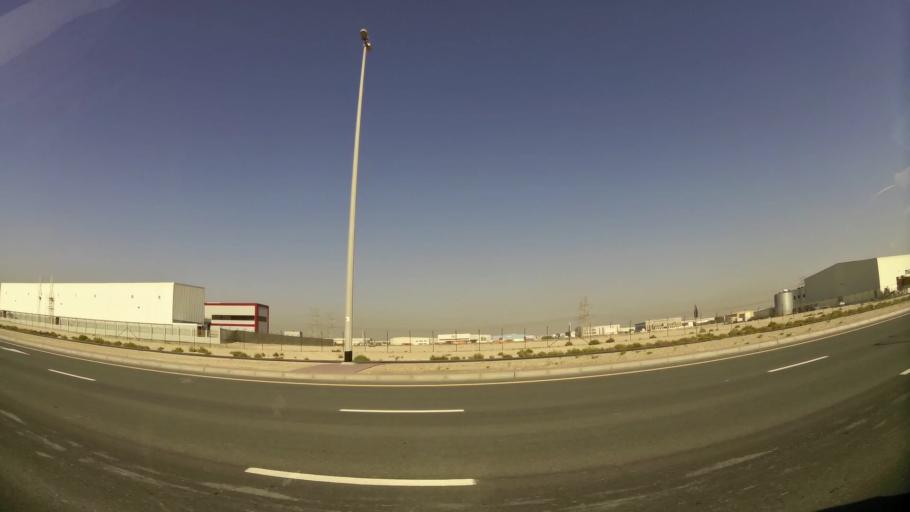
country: AE
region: Dubai
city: Dubai
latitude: 24.9767
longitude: 55.1130
